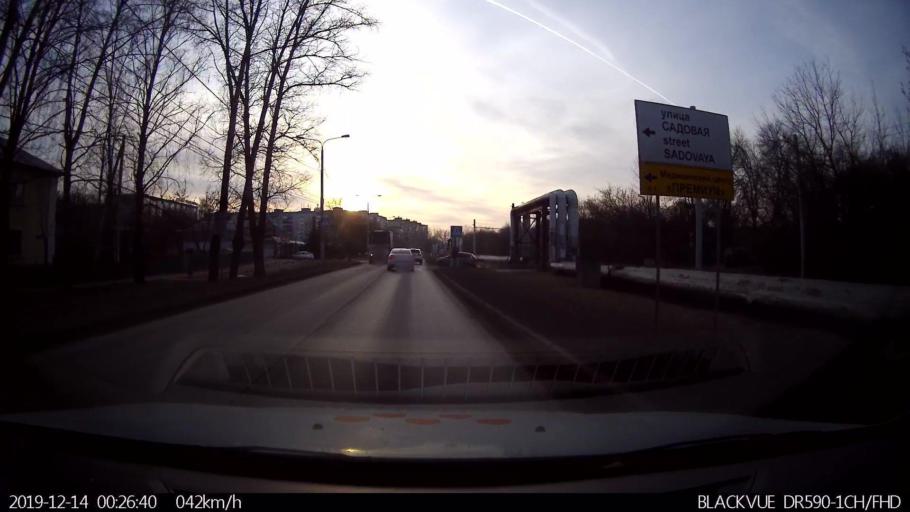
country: RU
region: Nizjnij Novgorod
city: Burevestnik
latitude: 56.2248
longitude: 43.8366
